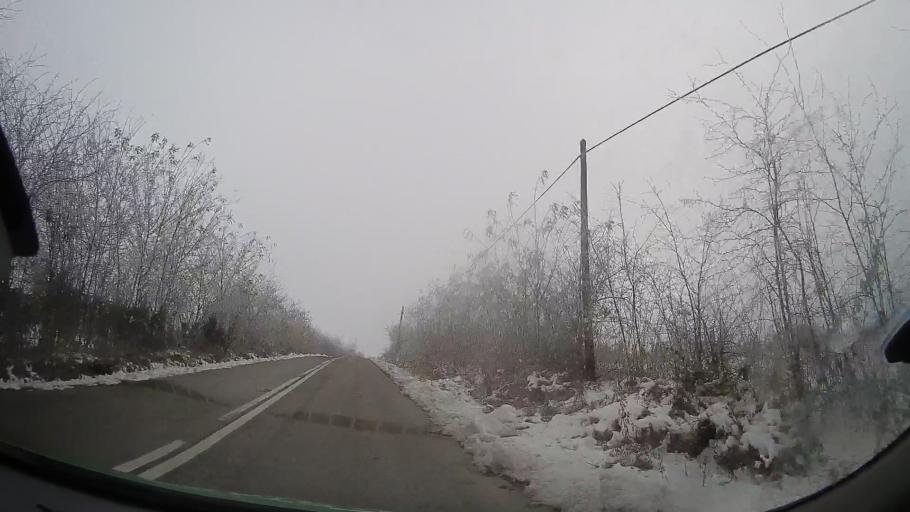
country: RO
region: Bacau
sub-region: Comuna Podu Turcului
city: Podu Turcului
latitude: 46.2075
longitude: 27.4027
